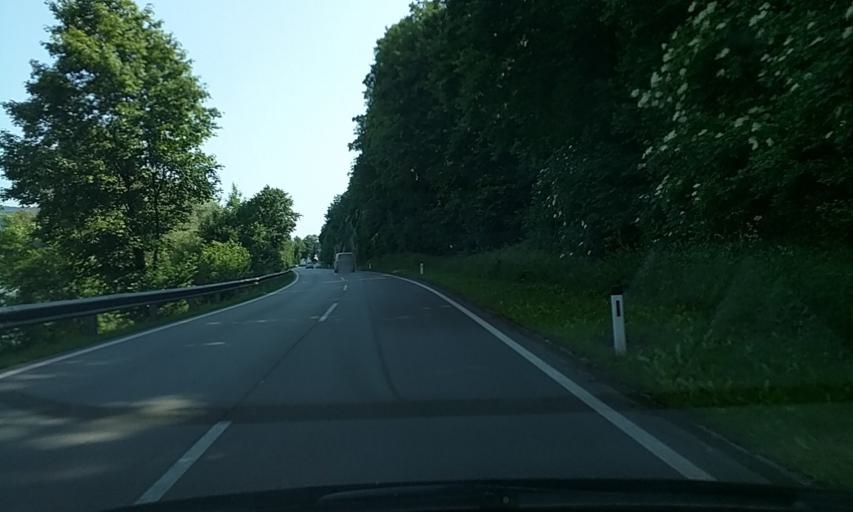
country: AT
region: Lower Austria
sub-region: Politischer Bezirk Melk
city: Emmersdorf an der Donau
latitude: 48.2431
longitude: 15.3516
